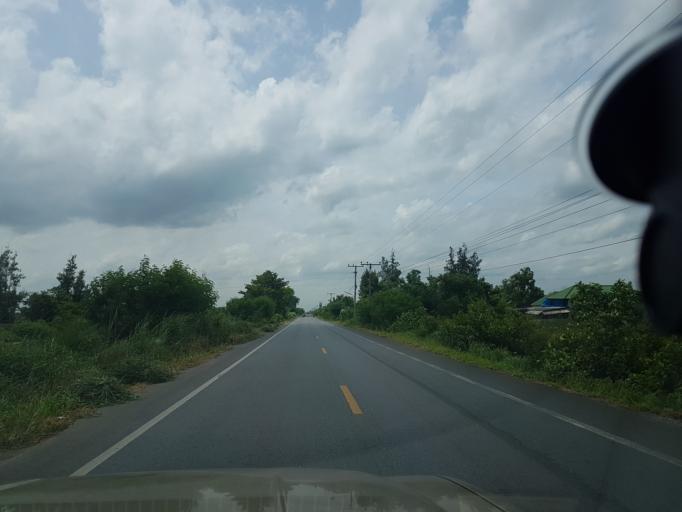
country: TH
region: Sara Buri
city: Nong Khae
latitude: 14.2626
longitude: 100.8919
